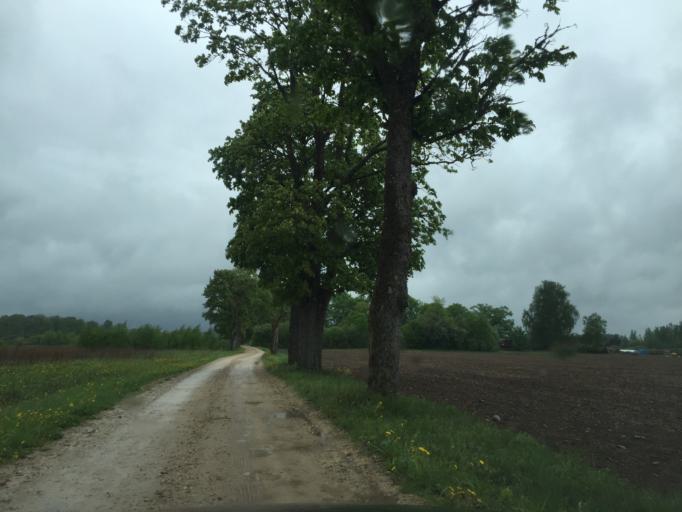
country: LV
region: Ogre
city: Jumprava
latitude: 56.6646
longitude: 25.0011
